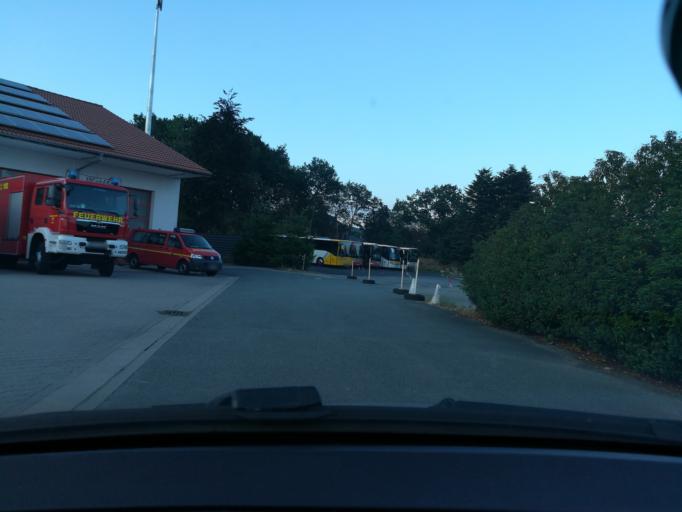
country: DE
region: North Rhine-Westphalia
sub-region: Regierungsbezirk Munster
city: Lienen
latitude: 52.1486
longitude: 7.9648
